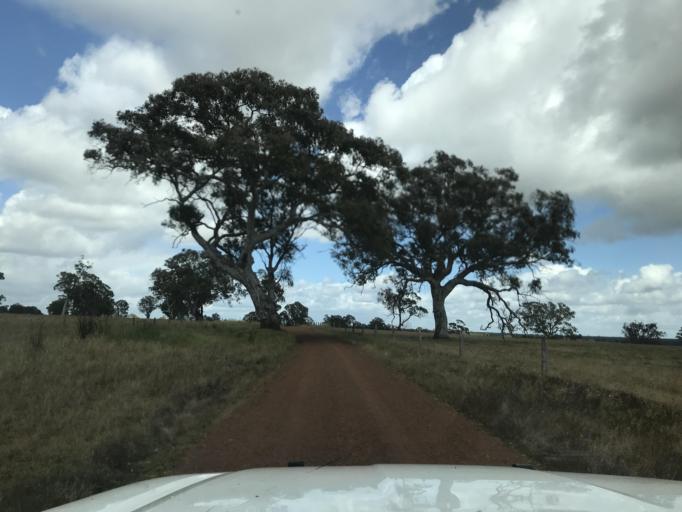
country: AU
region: South Australia
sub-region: Wattle Range
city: Penola
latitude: -37.1938
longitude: 141.4224
